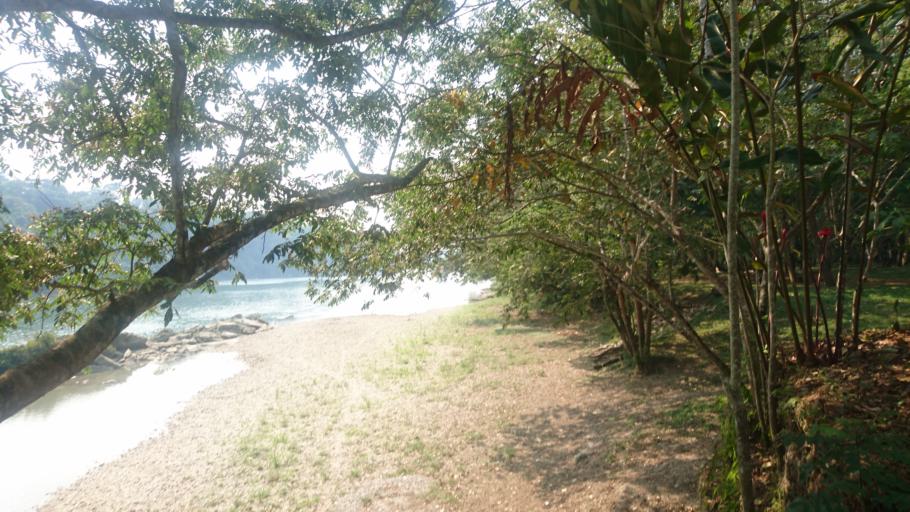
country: MX
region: Chiapas
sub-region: Marques de Comillas
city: Zamora Pico de Oro
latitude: 16.2572
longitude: -90.8629
